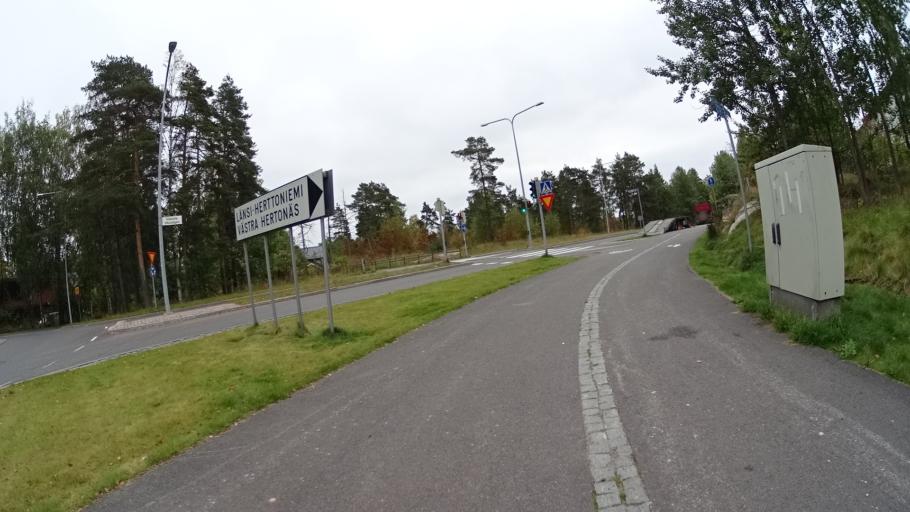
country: FI
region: Uusimaa
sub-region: Helsinki
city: Vantaa
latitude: 60.2148
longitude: 25.0445
